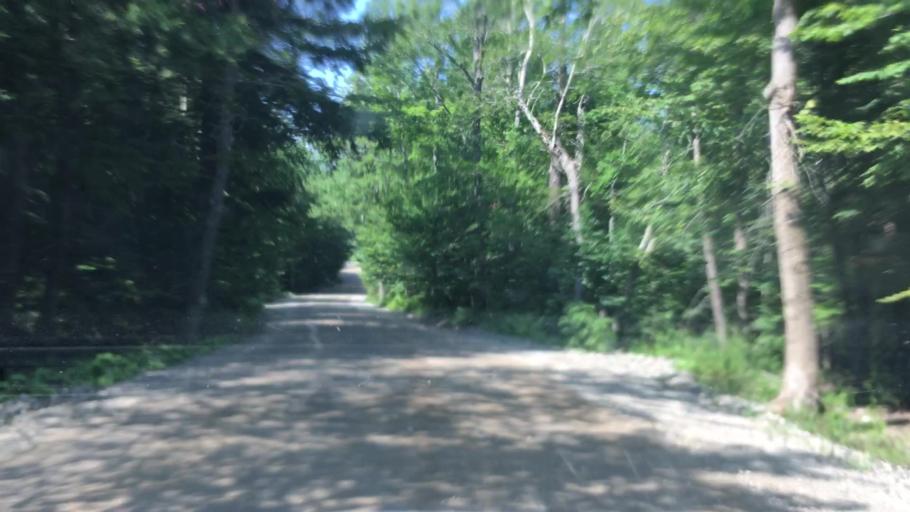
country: US
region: Maine
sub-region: Androscoggin County
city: Poland
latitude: 43.9877
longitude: -70.3866
